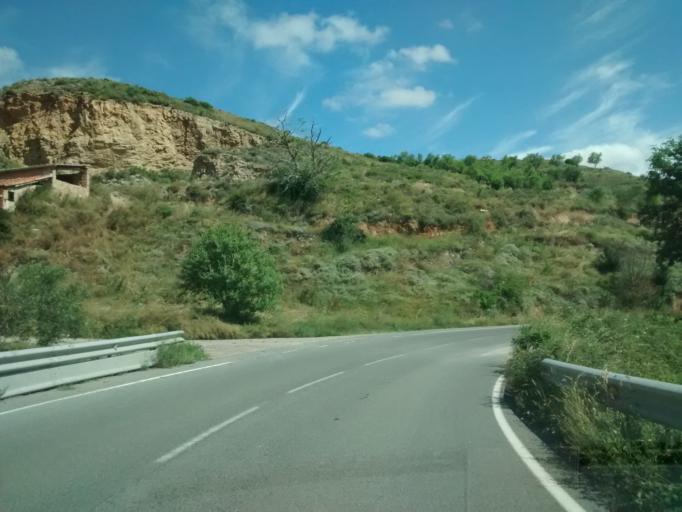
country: ES
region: La Rioja
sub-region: Provincia de La Rioja
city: Leza de Rio Leza
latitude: 42.3390
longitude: -2.4066
